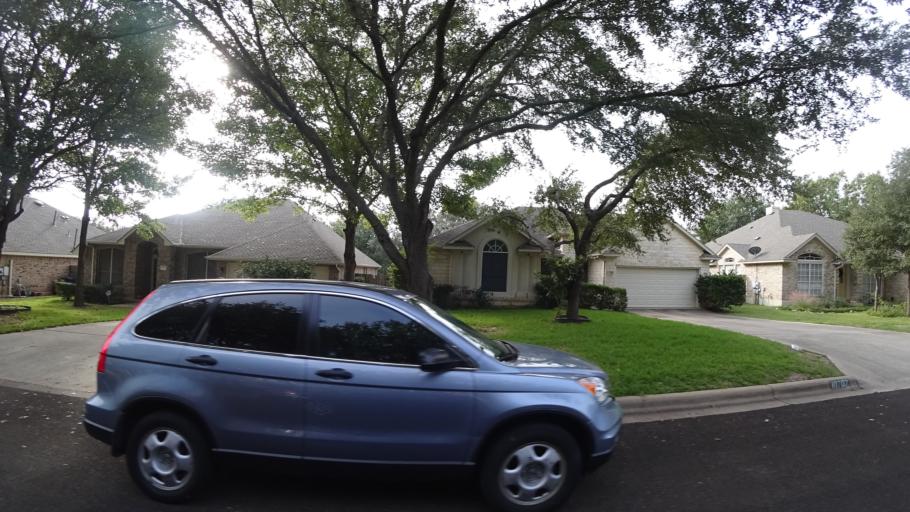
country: US
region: Texas
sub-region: Travis County
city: Shady Hollow
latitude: 30.1896
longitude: -97.8878
